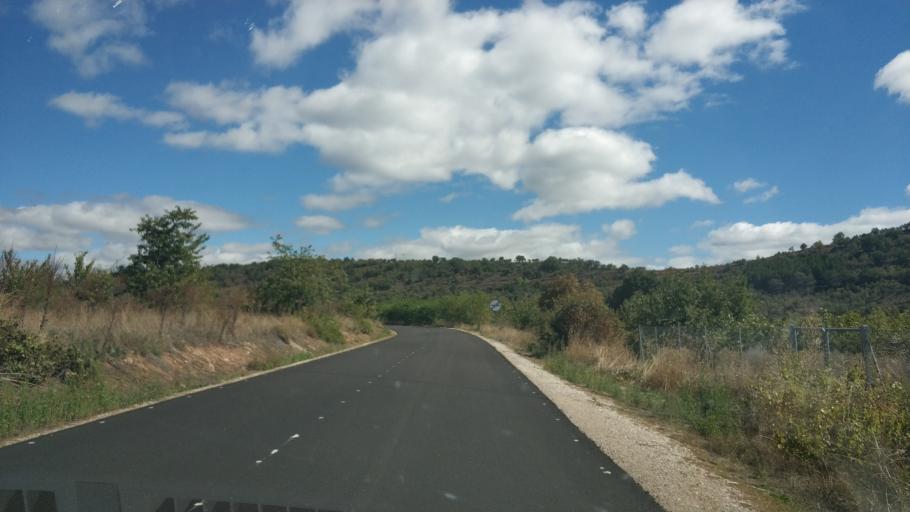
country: ES
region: Castille and Leon
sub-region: Provincia de Burgos
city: Covarrubias
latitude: 42.0482
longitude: -3.5296
